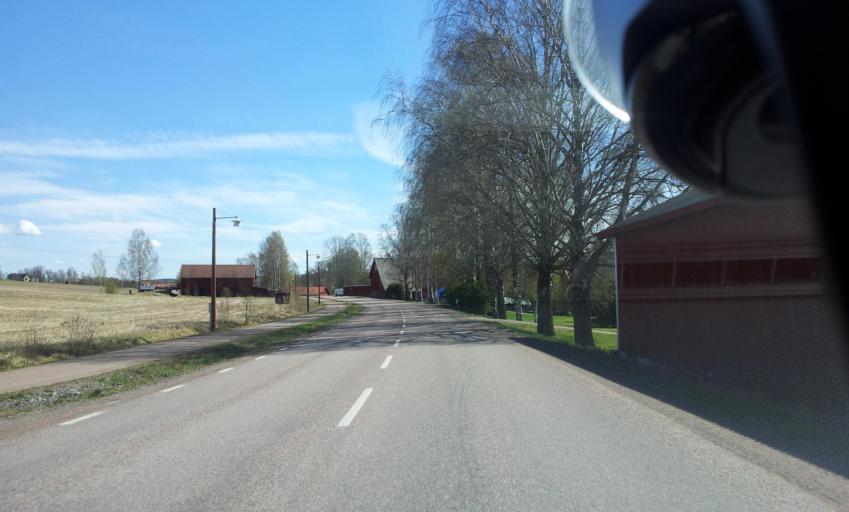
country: SE
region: Dalarna
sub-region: Borlange Kommun
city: Ornas
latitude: 60.4623
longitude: 15.5282
